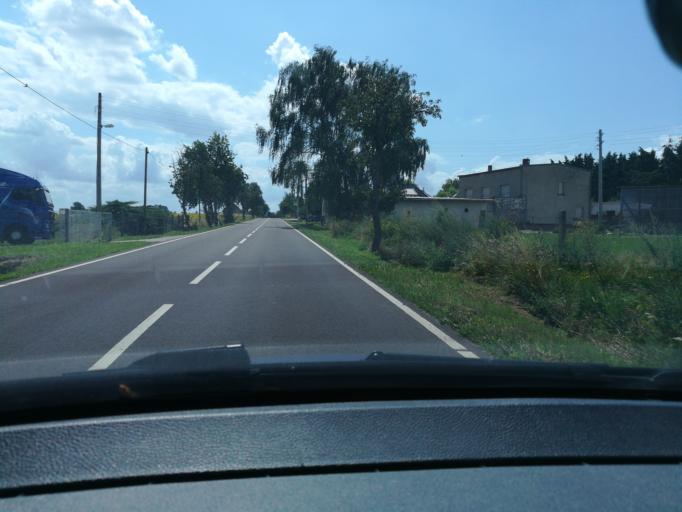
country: DE
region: Saxony-Anhalt
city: Rogatz
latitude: 52.3306
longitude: 11.7769
